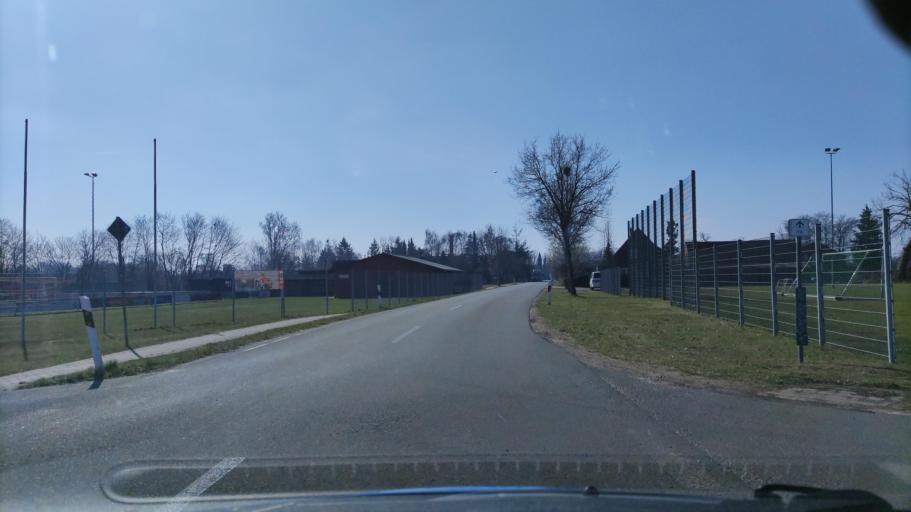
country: DE
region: Lower Saxony
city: Kusten
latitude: 52.9804
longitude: 11.0655
